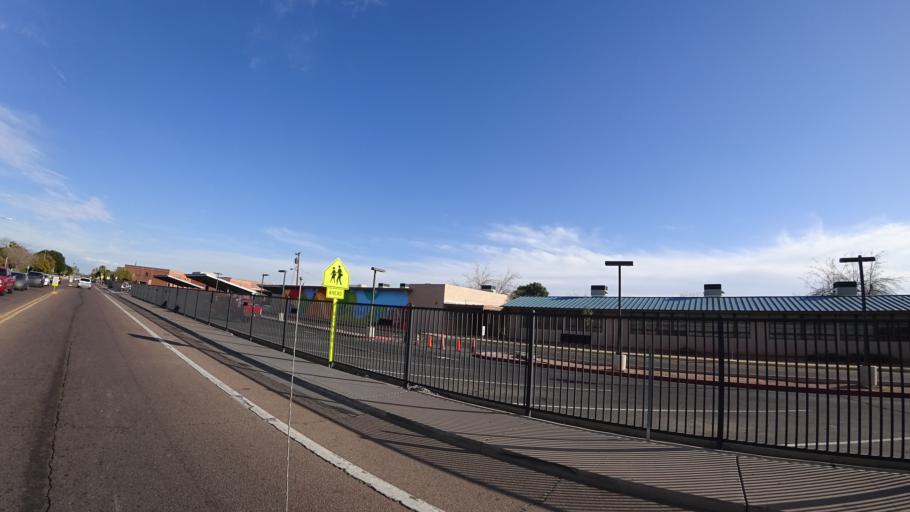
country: US
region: Arizona
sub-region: Maricopa County
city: Phoenix
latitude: 33.4586
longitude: -112.1418
